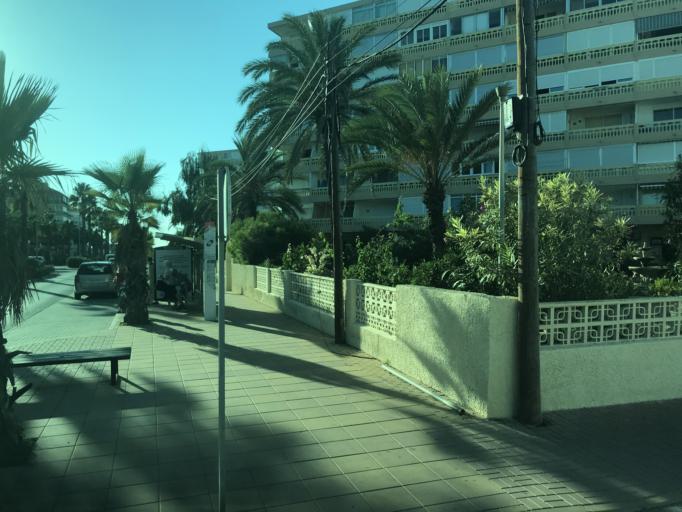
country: ES
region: Valencia
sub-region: Provincia de Alicante
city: Torrevieja
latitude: 38.0205
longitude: -0.6551
